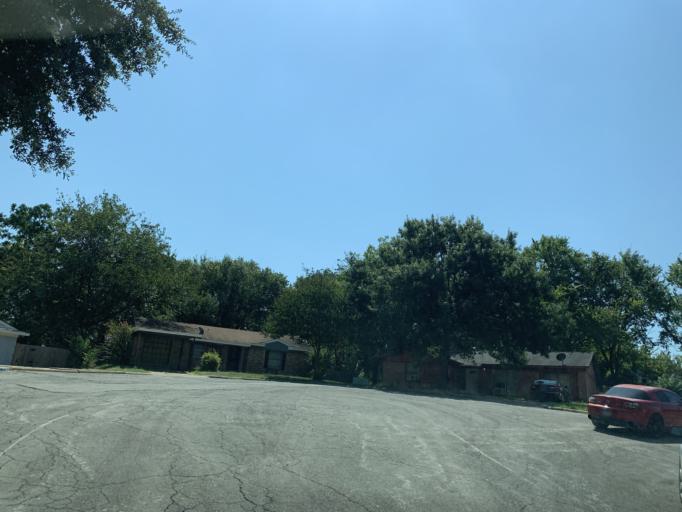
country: US
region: Texas
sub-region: Dallas County
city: Hutchins
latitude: 32.6758
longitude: -96.7540
